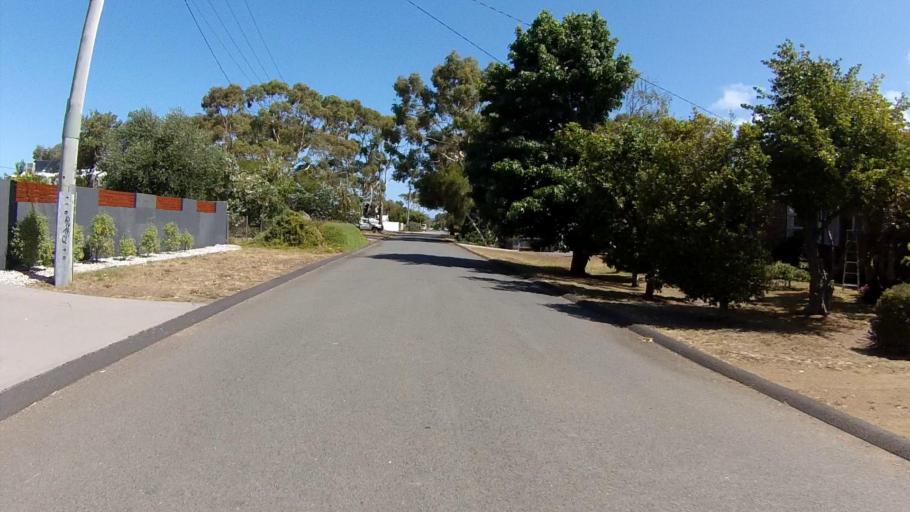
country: AU
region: Tasmania
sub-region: Clarence
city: Lauderdale
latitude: -42.8966
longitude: 147.4979
